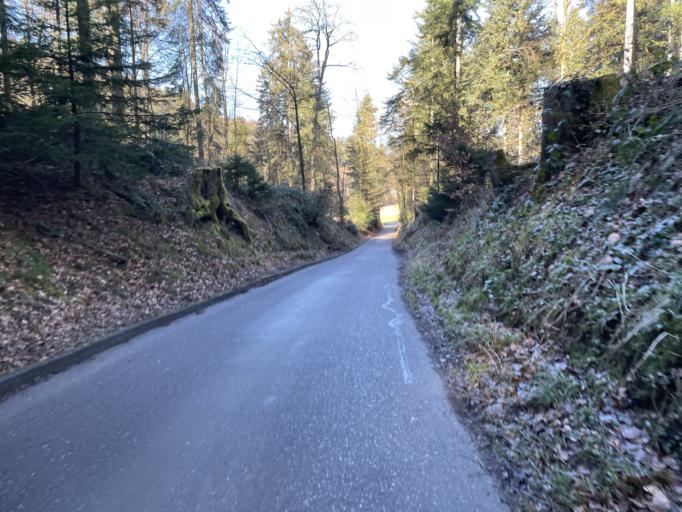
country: CH
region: Bern
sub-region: Bern-Mittelland District
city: Bariswil
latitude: 47.0091
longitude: 7.5354
